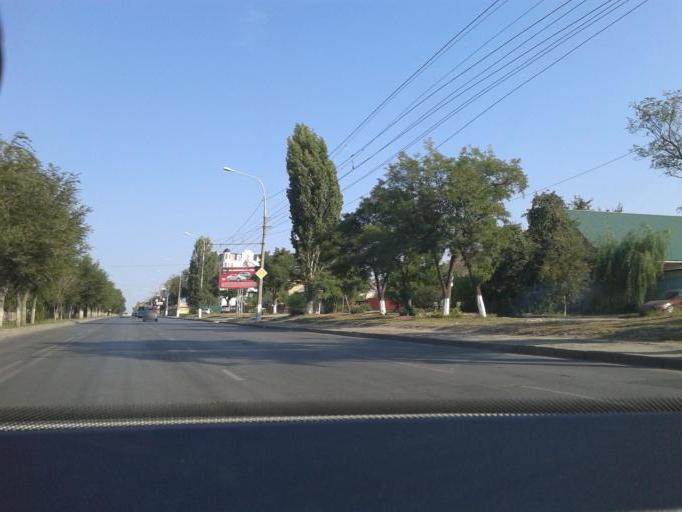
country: RU
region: Volgograd
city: Volgograd
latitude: 48.7245
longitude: 44.5016
